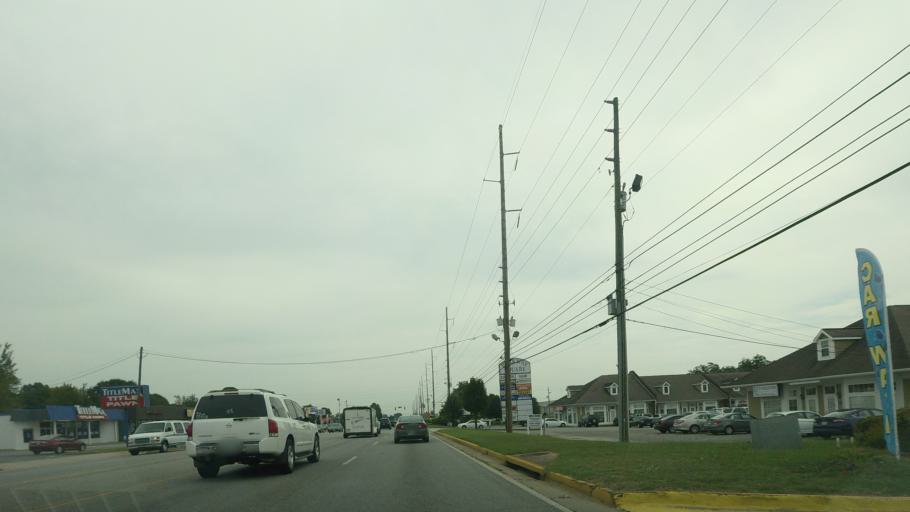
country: US
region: Georgia
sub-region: Houston County
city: Warner Robins
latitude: 32.5939
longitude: -83.6459
